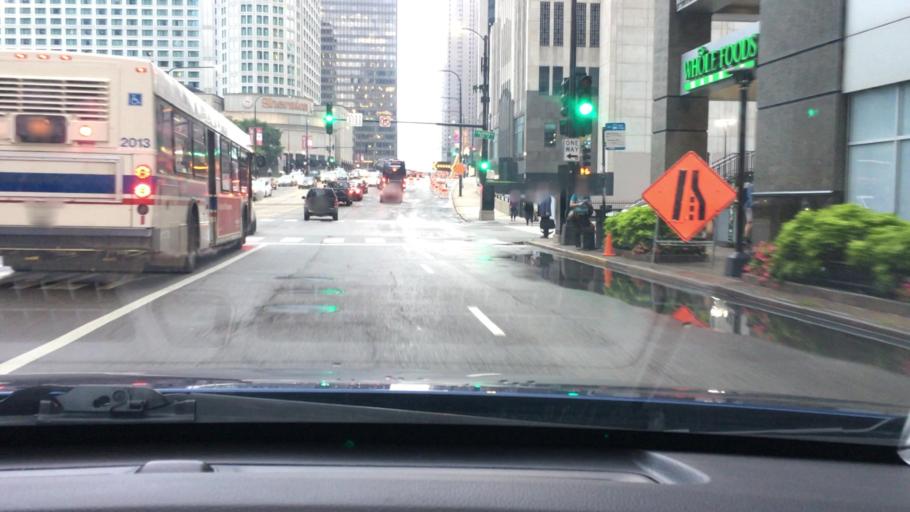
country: US
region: Illinois
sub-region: Cook County
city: Chicago
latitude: 41.8913
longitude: -87.6203
